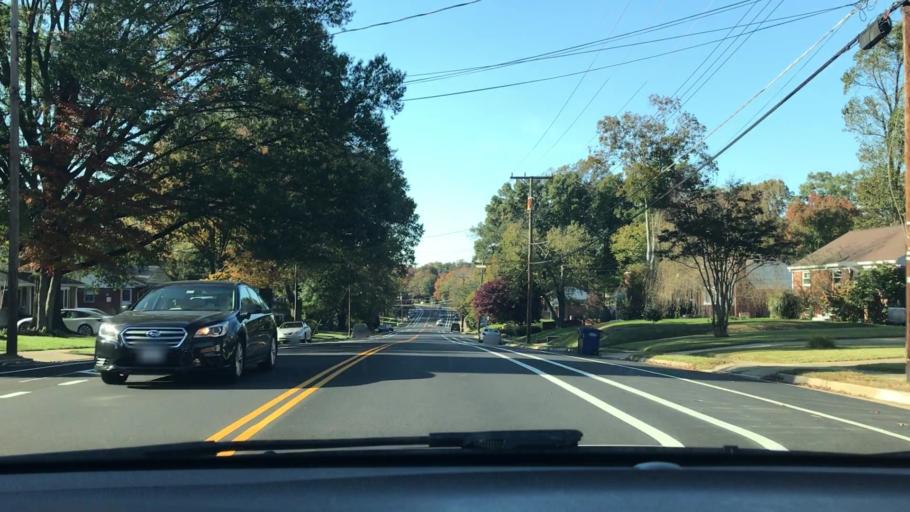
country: US
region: Virginia
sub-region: Fairfax County
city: Annandale
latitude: 38.8380
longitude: -77.1930
